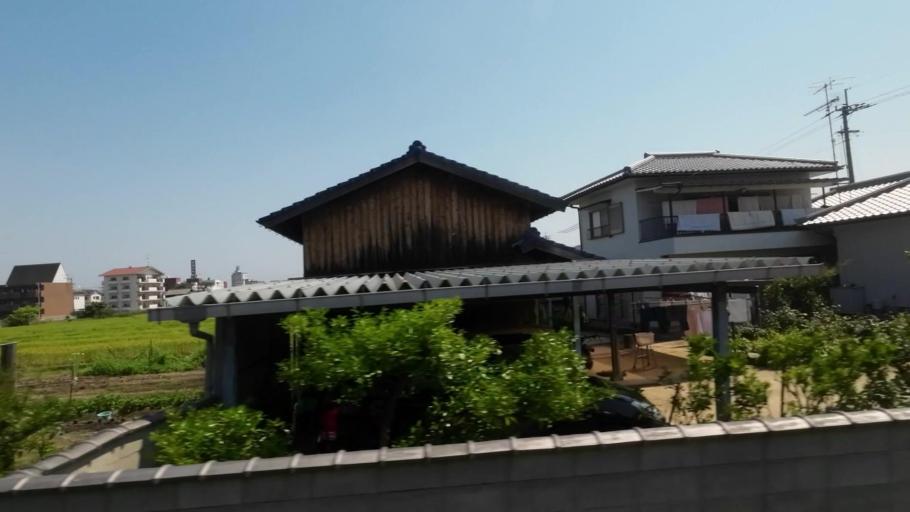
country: JP
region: Ehime
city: Saijo
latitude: 33.9263
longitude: 133.0886
